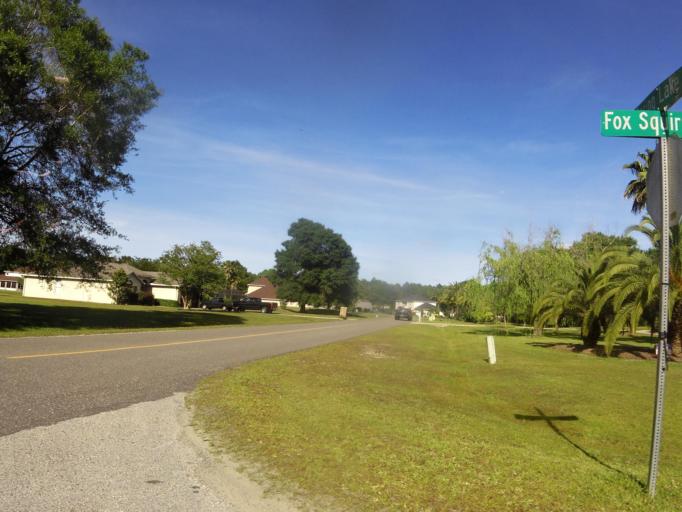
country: US
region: Florida
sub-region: Nassau County
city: Callahan
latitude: 30.5615
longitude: -81.7810
